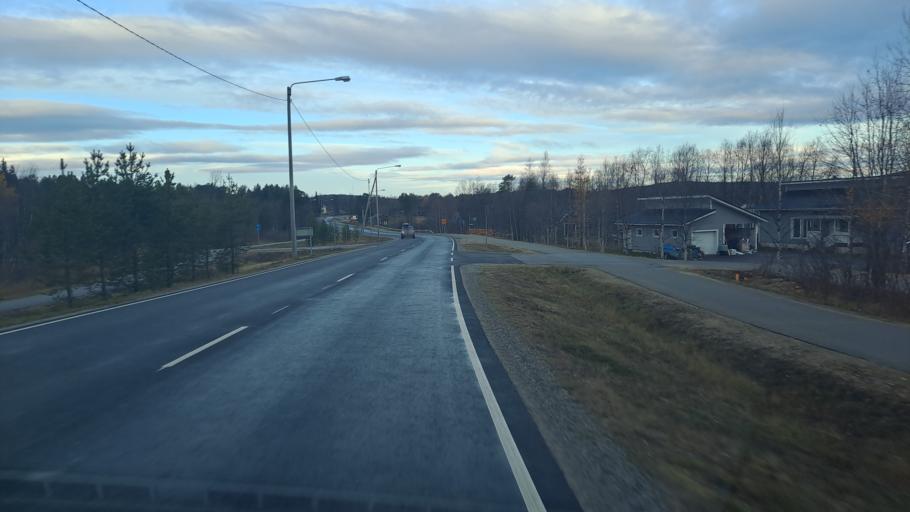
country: FI
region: Lapland
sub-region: Pohjois-Lappi
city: Inari
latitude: 68.9009
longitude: 27.0441
